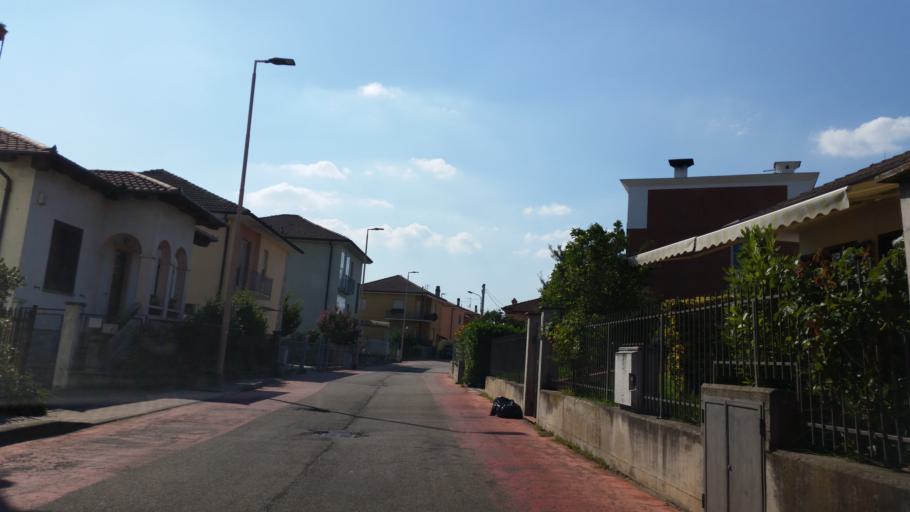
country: IT
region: Piedmont
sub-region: Provincia di Cuneo
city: Alba
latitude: 44.6995
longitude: 8.0181
